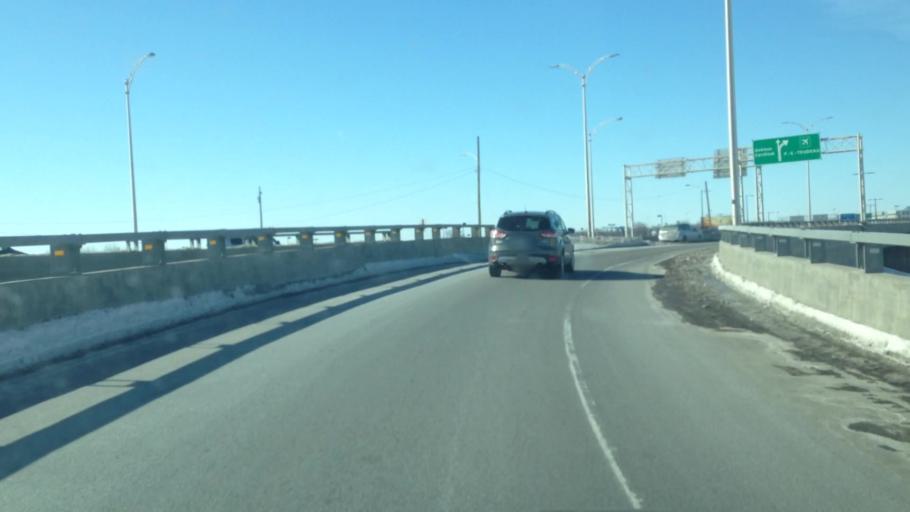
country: CA
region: Quebec
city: Dorval
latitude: 45.4521
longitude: -73.7407
